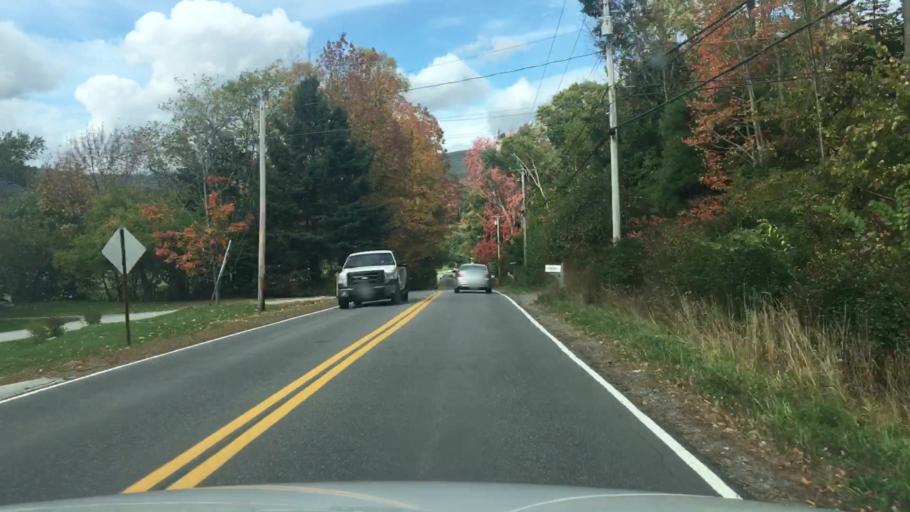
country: US
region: Maine
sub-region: Knox County
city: Camden
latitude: 44.2094
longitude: -69.0913
